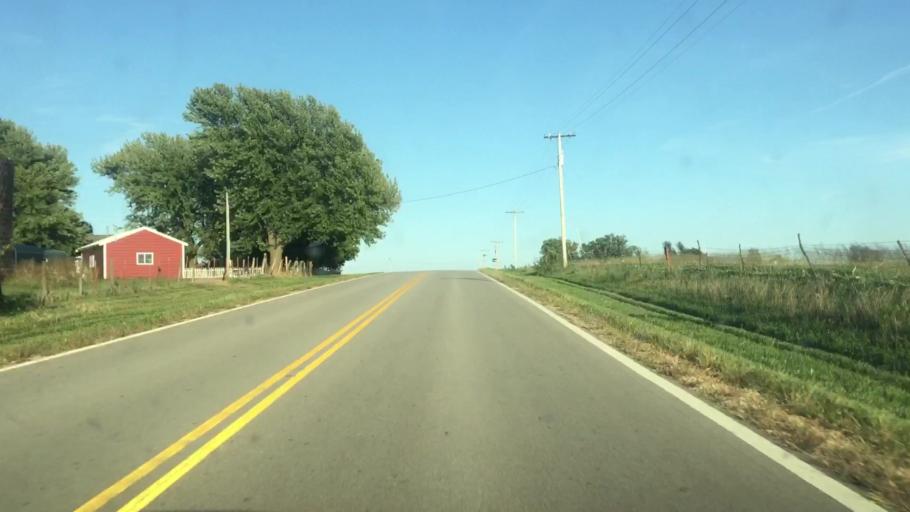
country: US
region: Kansas
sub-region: Brown County
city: Horton
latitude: 39.5876
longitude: -95.5858
